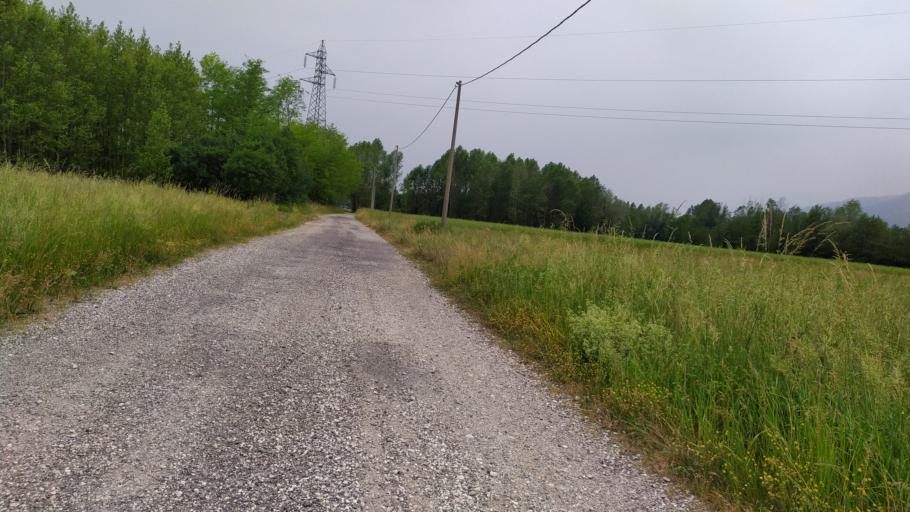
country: IT
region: Friuli Venezia Giulia
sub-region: Provincia di Udine
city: Majano
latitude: 46.2137
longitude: 13.0566
